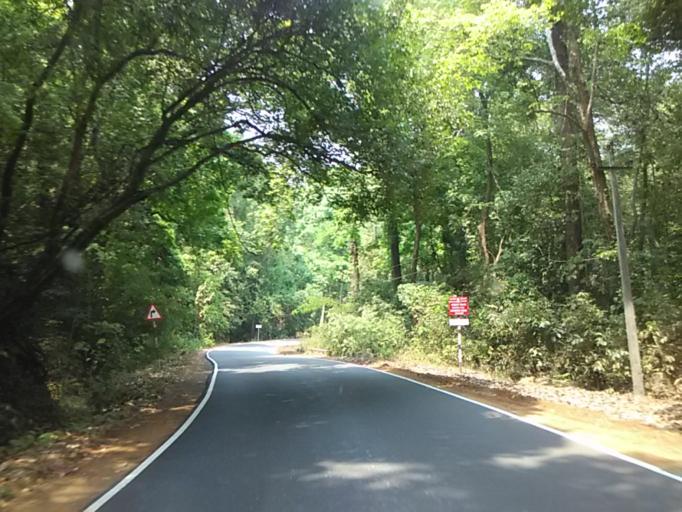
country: IN
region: Karnataka
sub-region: Kodagu
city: Virarajendrapet
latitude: 12.0818
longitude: 75.7380
